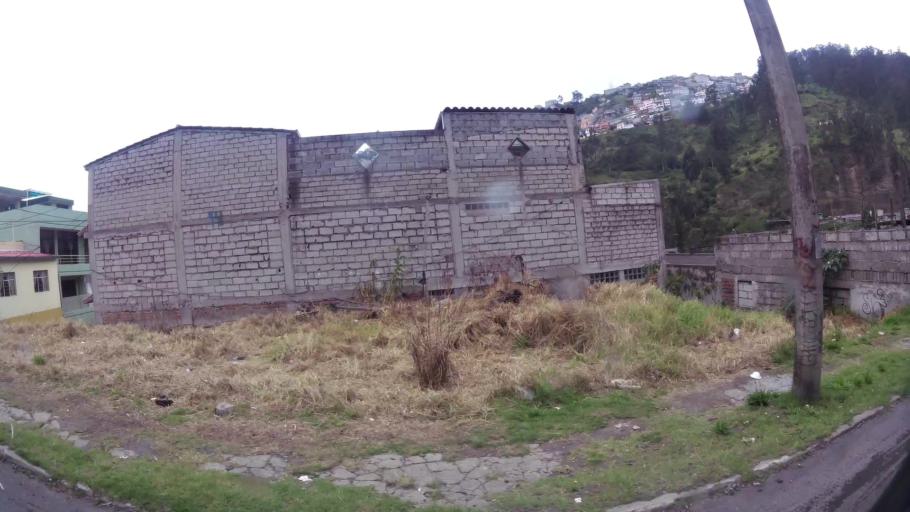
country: EC
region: Pichincha
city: Quito
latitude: -0.2296
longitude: -78.5007
